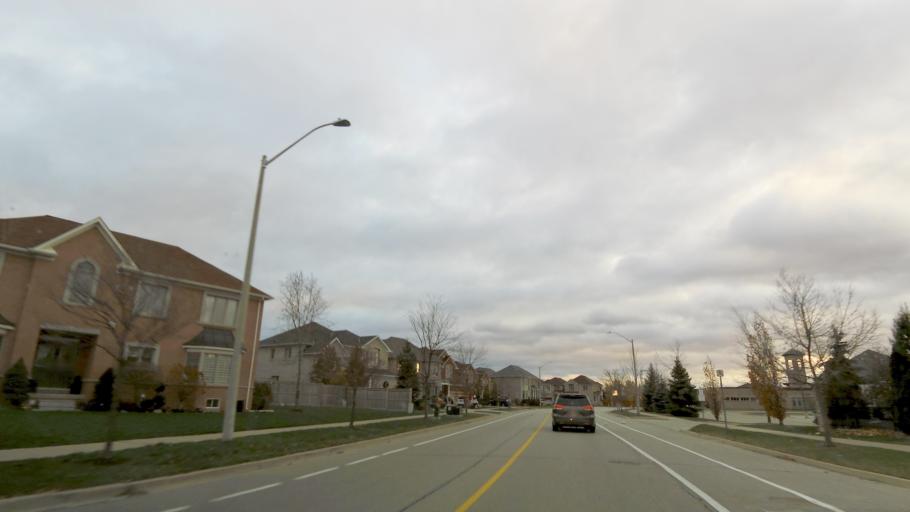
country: CA
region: Ontario
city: Oakville
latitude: 43.4902
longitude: -79.7120
